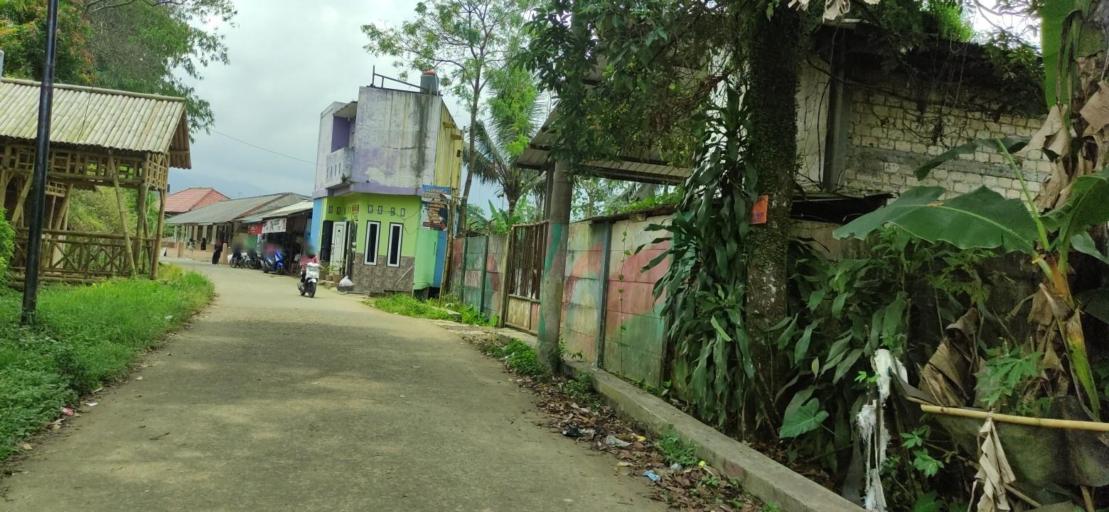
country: ID
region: West Java
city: Caringin
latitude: -6.6438
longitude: 106.8960
